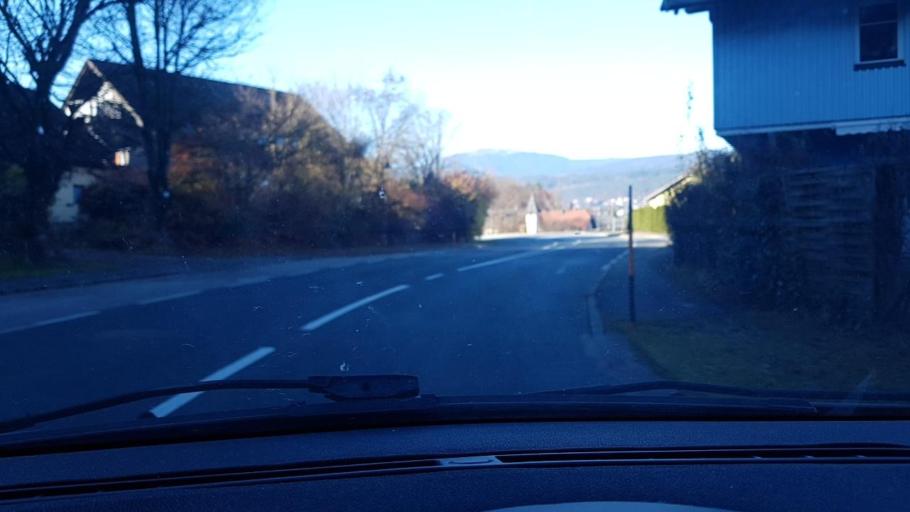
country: AT
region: Carinthia
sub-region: Politischer Bezirk Villach Land
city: Velden am Woerthersee
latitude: 46.6031
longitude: 14.0572
